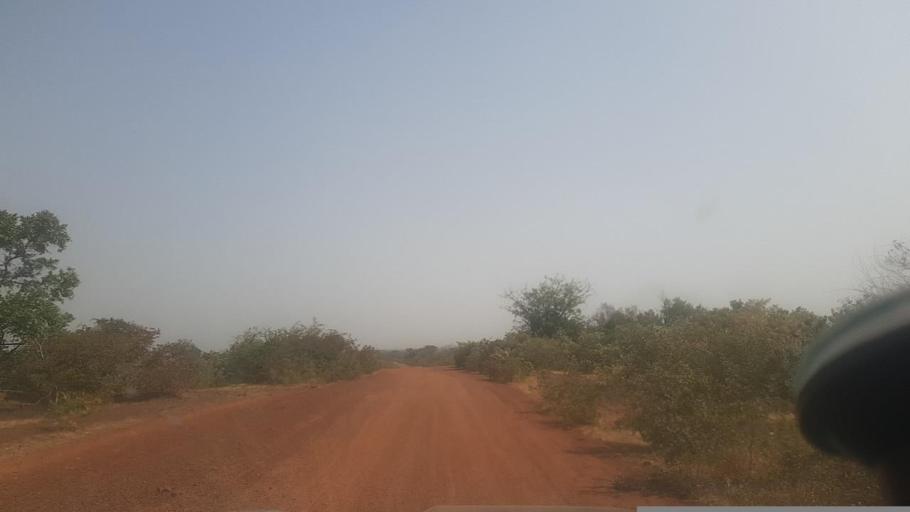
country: ML
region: Segou
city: Segou
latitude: 12.9272
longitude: -6.2743
